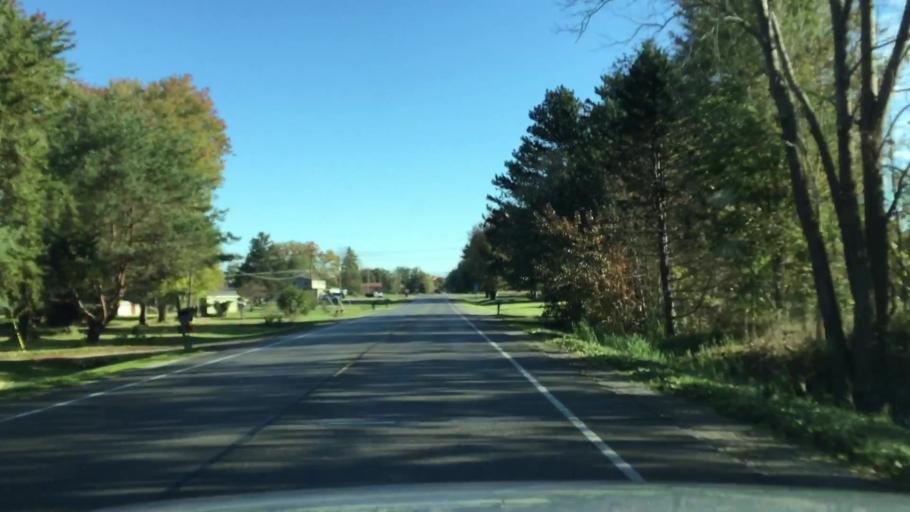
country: US
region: Michigan
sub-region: Shiawassee County
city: Durand
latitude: 42.9477
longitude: -83.9321
